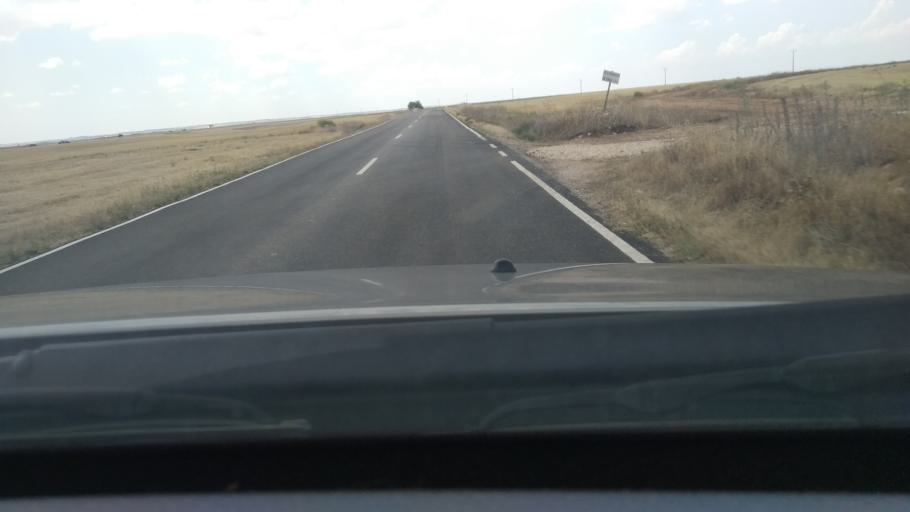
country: ES
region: Castille and Leon
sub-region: Provincia de Burgos
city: Iglesiarrubia
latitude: 41.9444
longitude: -3.8553
